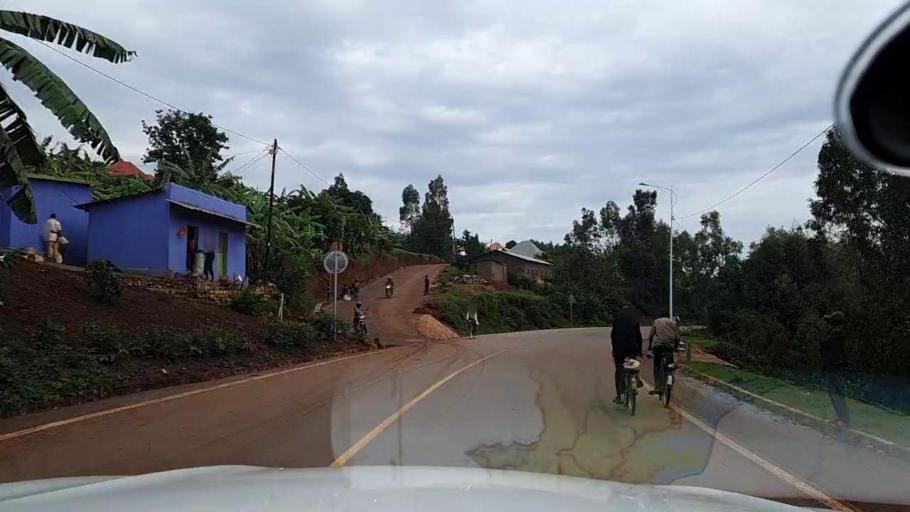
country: RW
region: Southern Province
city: Butare
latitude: -2.5791
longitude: 29.7339
